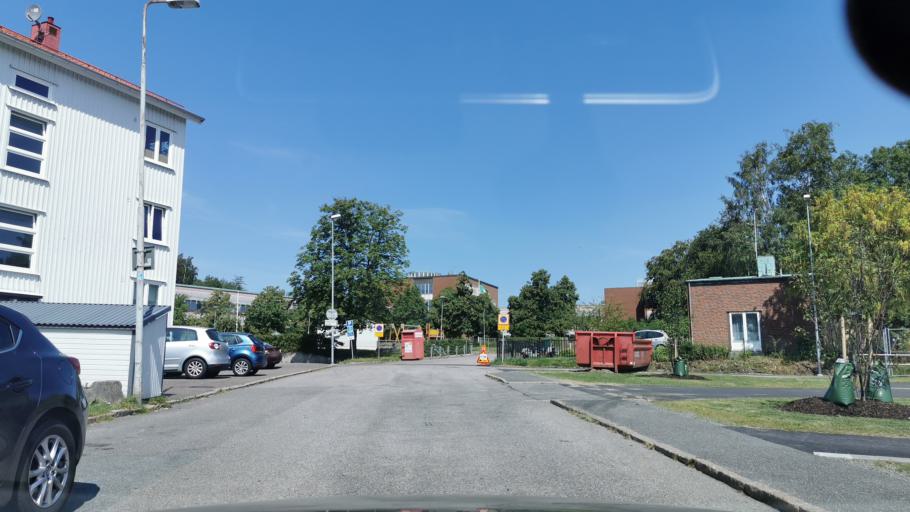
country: SE
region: Vaestra Goetaland
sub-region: Molndal
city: Moelndal
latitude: 57.6759
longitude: 11.9948
